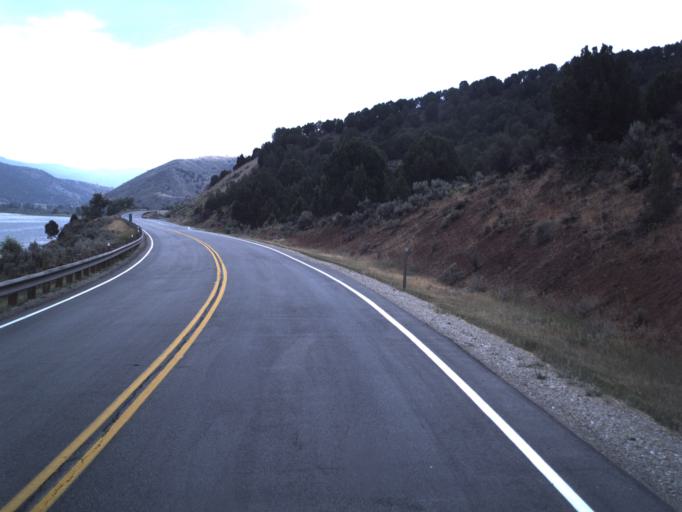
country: US
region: Utah
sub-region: Summit County
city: Oakley
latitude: 40.7631
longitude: -111.3972
